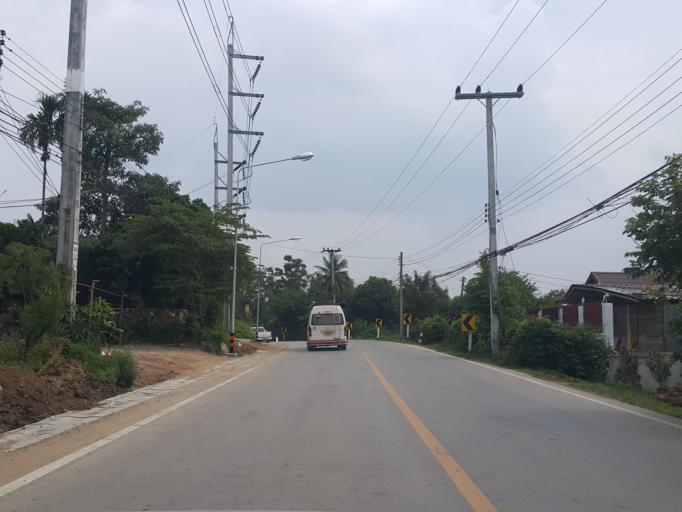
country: TH
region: Chiang Mai
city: Mae Taeng
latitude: 19.0952
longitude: 98.8494
